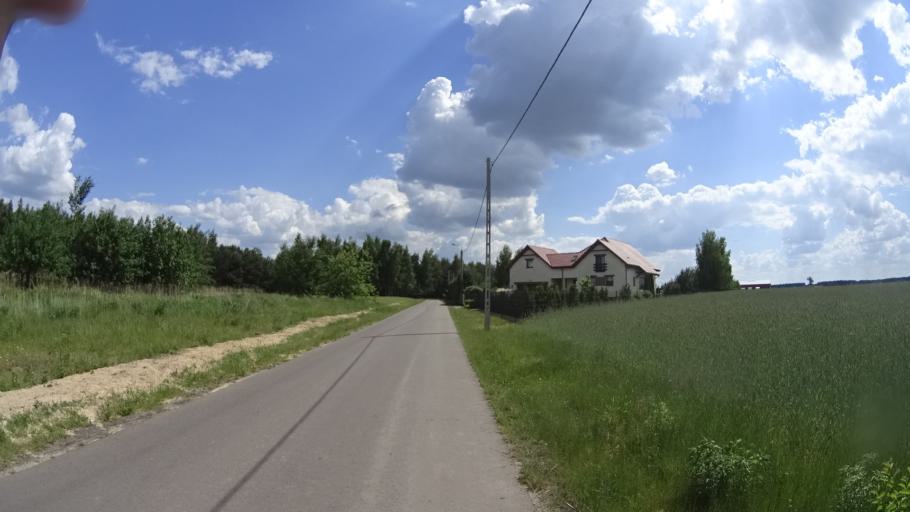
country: PL
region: Masovian Voivodeship
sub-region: Powiat piaseczynski
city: Tarczyn
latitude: 52.0157
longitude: 20.8183
